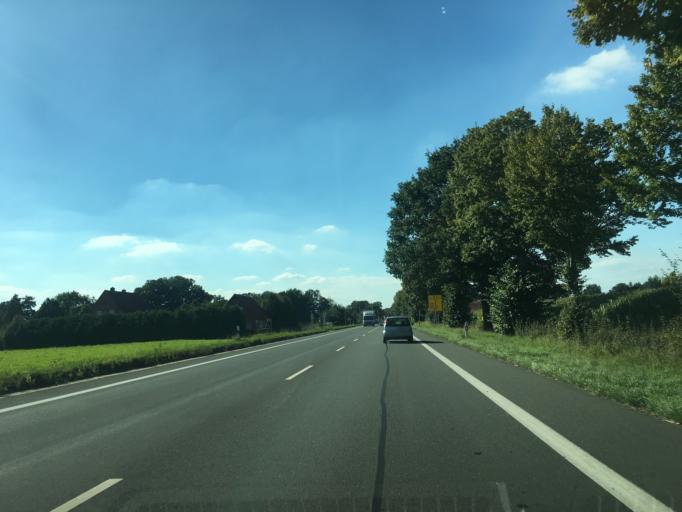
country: DE
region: North Rhine-Westphalia
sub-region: Regierungsbezirk Munster
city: Beelen
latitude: 51.9266
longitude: 8.1304
